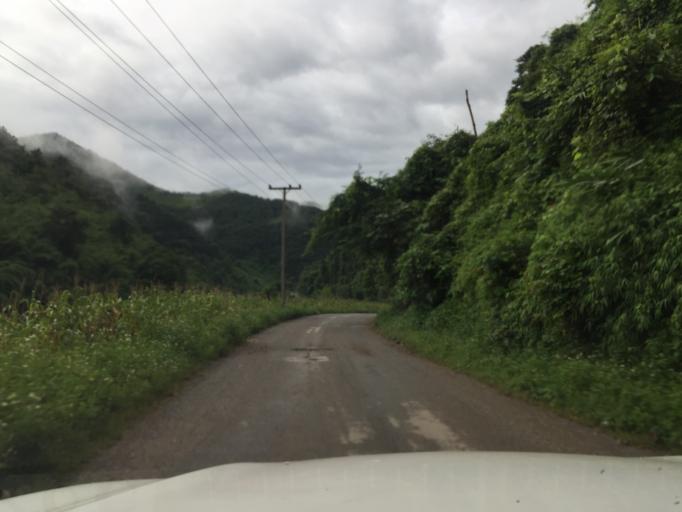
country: LA
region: Oudomxai
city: Muang La
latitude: 21.0802
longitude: 102.2423
